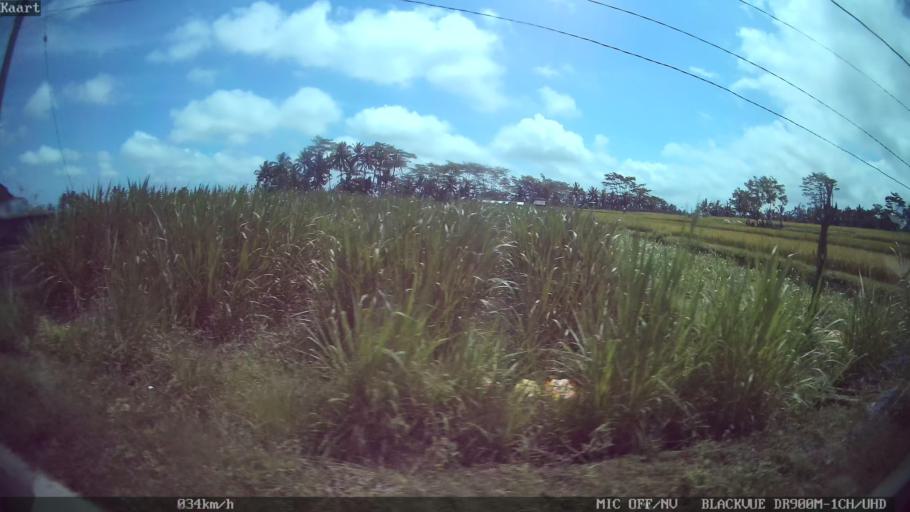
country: ID
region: Bali
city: Banjar Apuan Kaja
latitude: -8.4956
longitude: 115.3415
